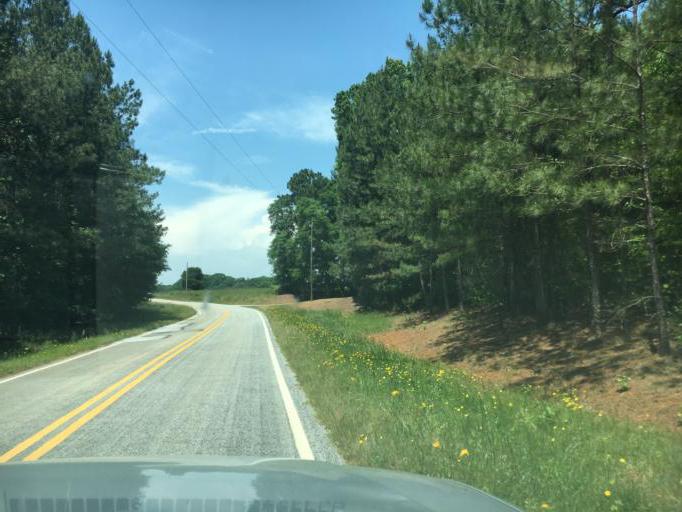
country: US
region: Georgia
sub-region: Hart County
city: Royston
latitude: 34.3156
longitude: -83.0922
